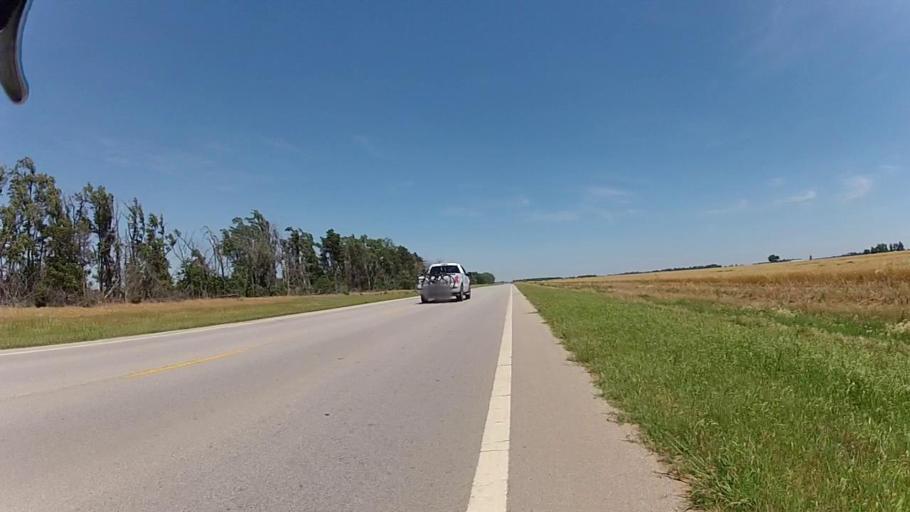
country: US
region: Kansas
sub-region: Harper County
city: Harper
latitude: 37.2389
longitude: -98.1565
